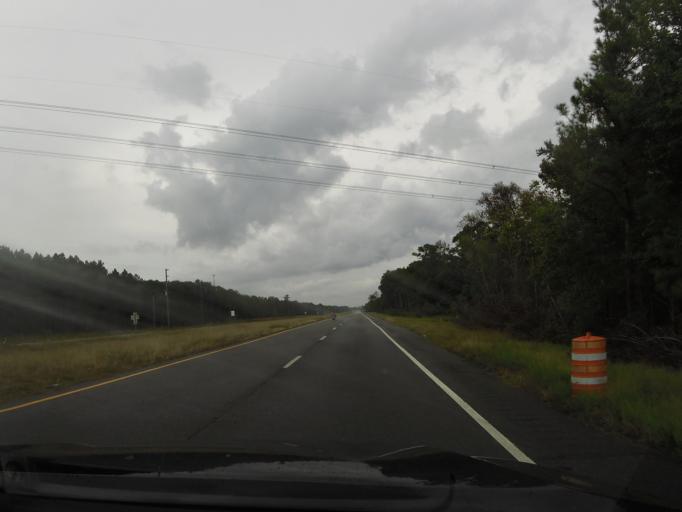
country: US
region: Georgia
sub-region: McIntosh County
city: Darien
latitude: 31.4075
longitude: -81.6556
